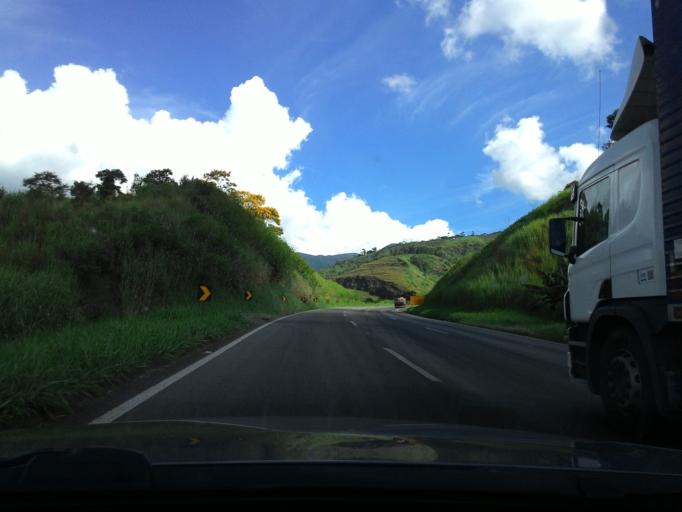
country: BR
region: Sao Paulo
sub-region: Cajati
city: Cajati
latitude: -24.8446
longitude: -48.2197
